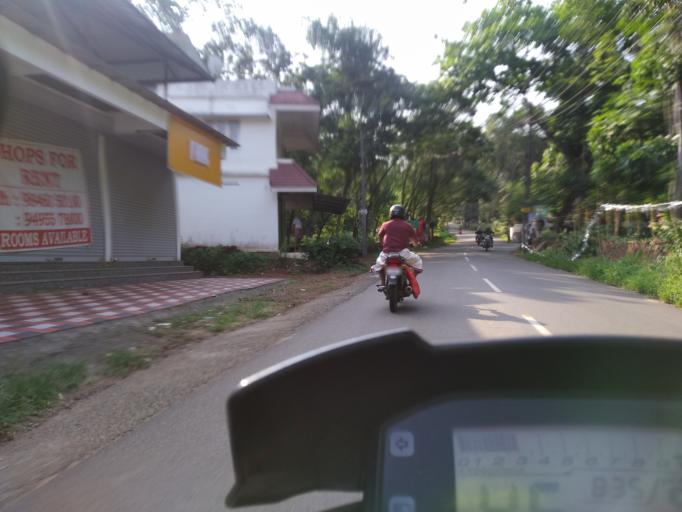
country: IN
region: Kerala
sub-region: Ernakulam
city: Ramamangalam
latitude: 9.9139
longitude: 76.4242
